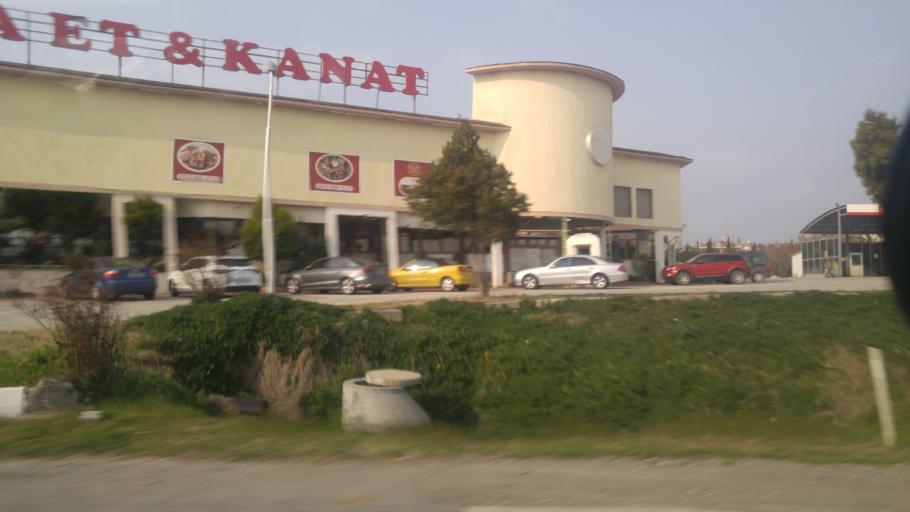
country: TR
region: Istanbul
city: Chekmejeh
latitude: 41.0091
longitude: 28.5230
